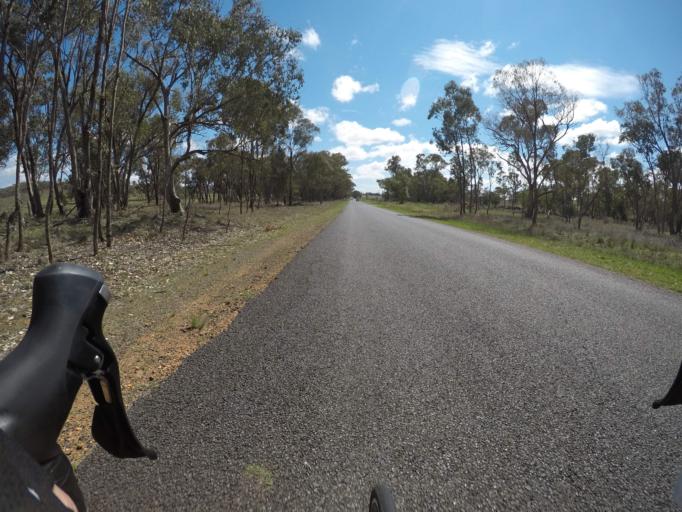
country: AU
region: New South Wales
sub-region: Dubbo Municipality
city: Dubbo
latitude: -32.5317
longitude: 148.5503
